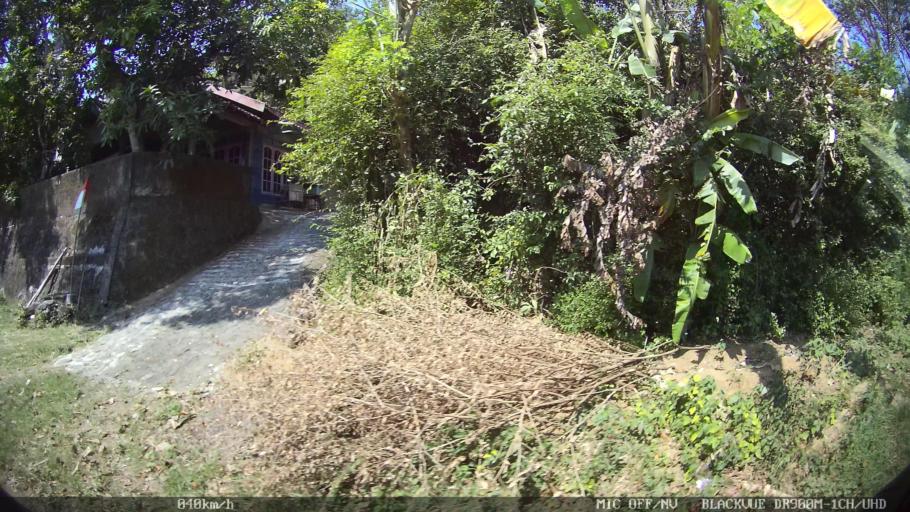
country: ID
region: Daerah Istimewa Yogyakarta
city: Pundong
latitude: -7.9563
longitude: 110.3795
